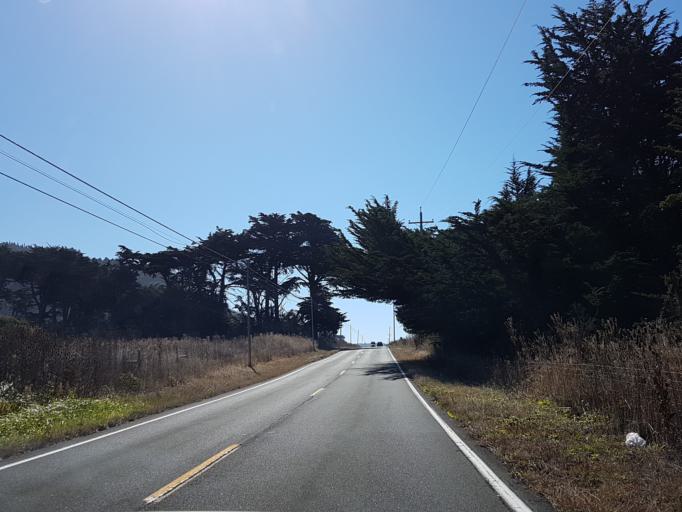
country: US
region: California
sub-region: Mendocino County
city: Boonville
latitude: 39.0889
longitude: -123.7006
